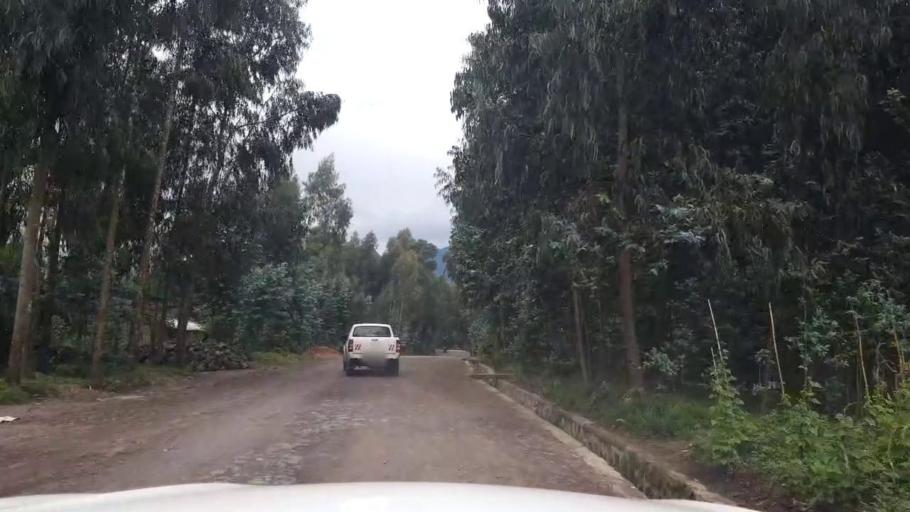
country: RW
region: Northern Province
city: Musanze
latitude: -1.4446
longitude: 29.5330
